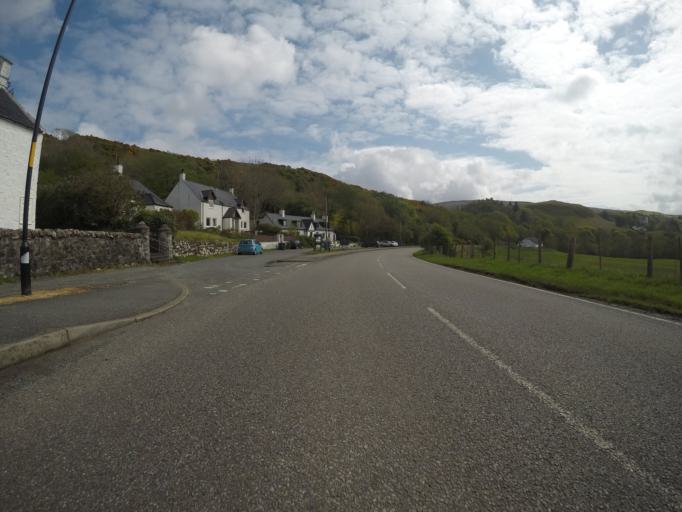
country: GB
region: Scotland
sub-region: Highland
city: Portree
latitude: 57.5916
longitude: -6.3564
